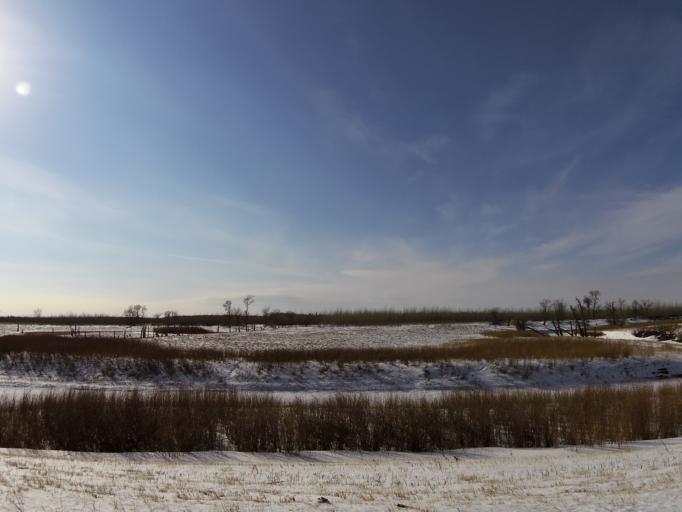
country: US
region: North Dakota
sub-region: Walsh County
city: Grafton
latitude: 48.4186
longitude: -97.1073
